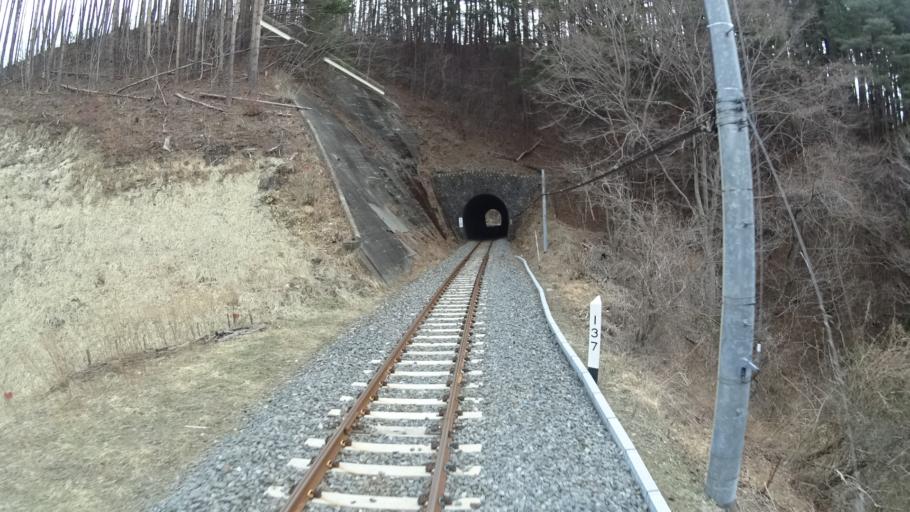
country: JP
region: Iwate
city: Otsuchi
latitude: 39.3964
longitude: 141.9465
